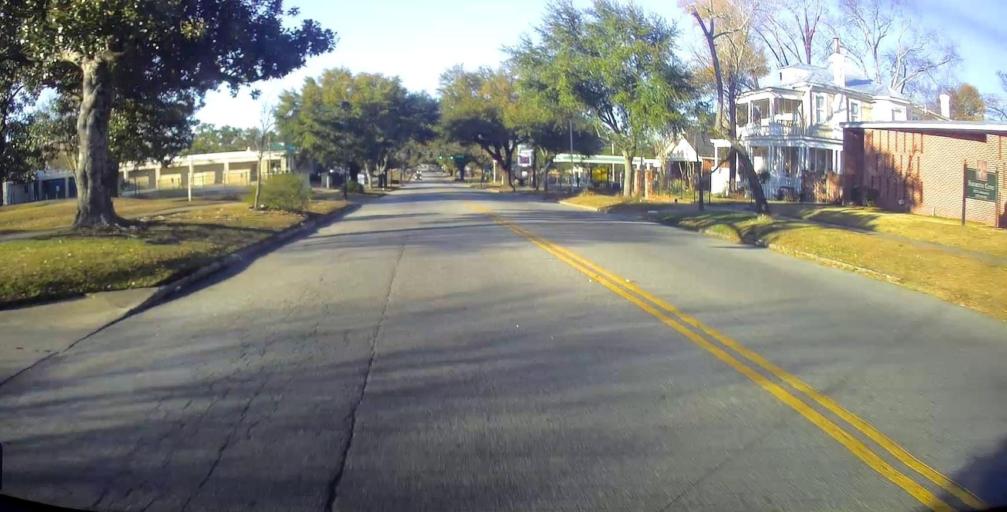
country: US
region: Georgia
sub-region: Dougherty County
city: Albany
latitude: 31.5874
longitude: -84.1561
